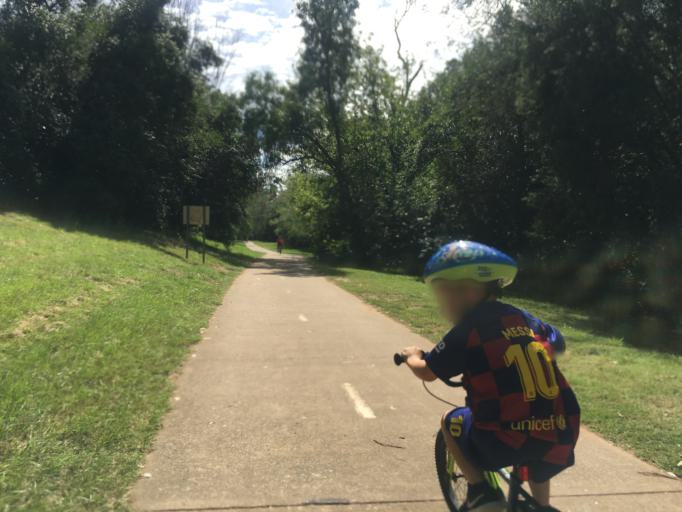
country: AU
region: New South Wales
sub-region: Camden
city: Camden South
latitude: -34.0756
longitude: 150.7010
